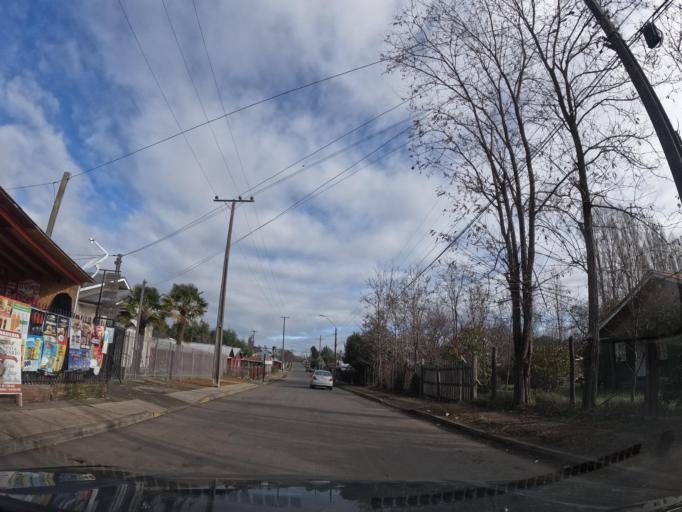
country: CL
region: Biobio
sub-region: Provincia de Nuble
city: Coihueco
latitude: -36.6995
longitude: -71.8976
